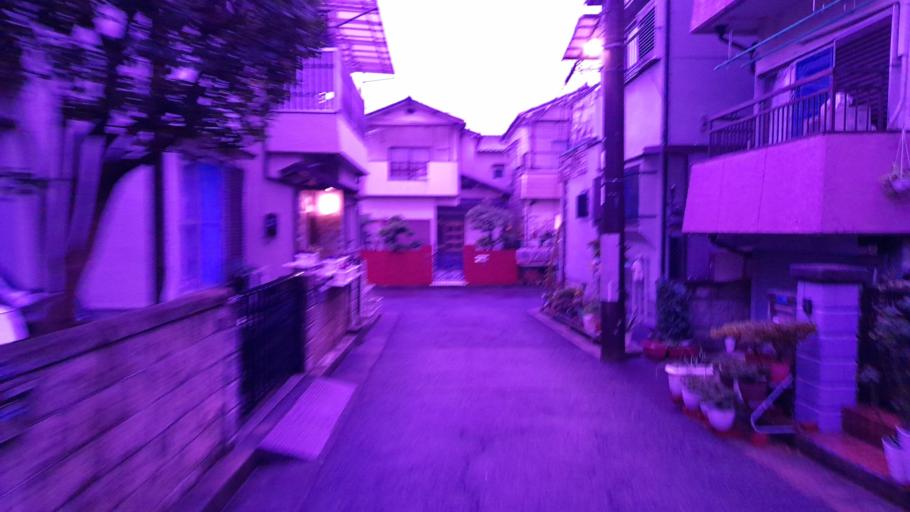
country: JP
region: Osaka
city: Toyonaka
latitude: 34.7456
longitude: 135.4515
